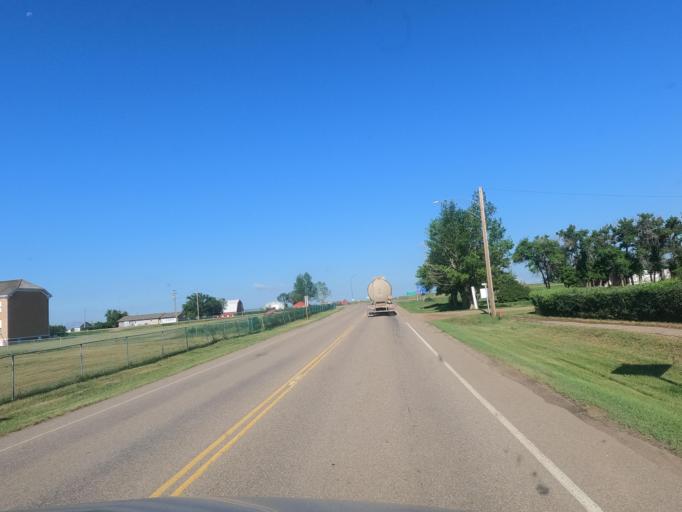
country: CA
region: Saskatchewan
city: Swift Current
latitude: 49.7278
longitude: -107.7417
